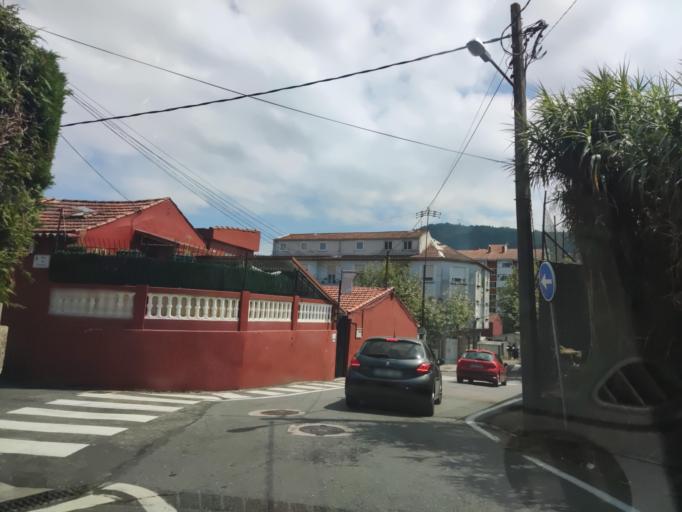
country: ES
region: Galicia
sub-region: Provincia de Pontevedra
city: Vigo
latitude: 42.2524
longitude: -8.6947
